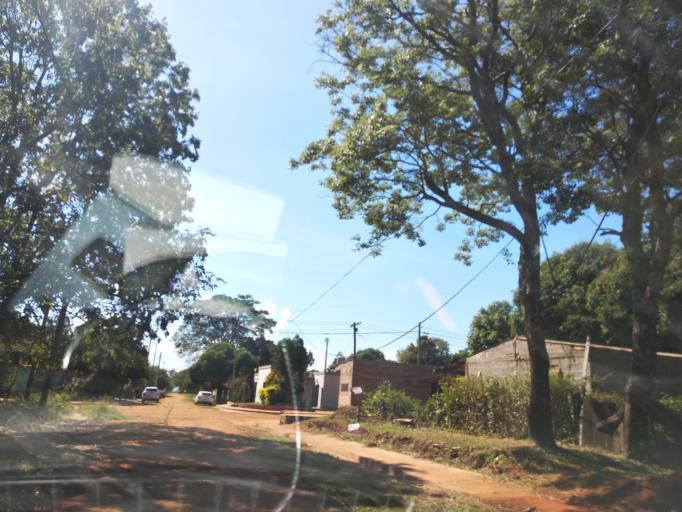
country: AR
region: Misiones
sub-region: Departamento de Capital
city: Posadas
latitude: -27.4278
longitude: -55.8849
